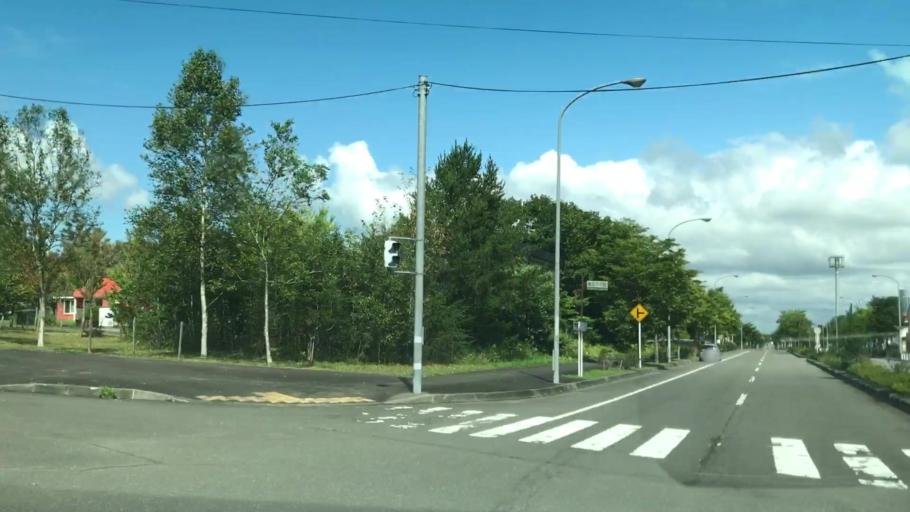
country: JP
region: Hokkaido
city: Chitose
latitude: 42.7750
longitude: 141.5994
